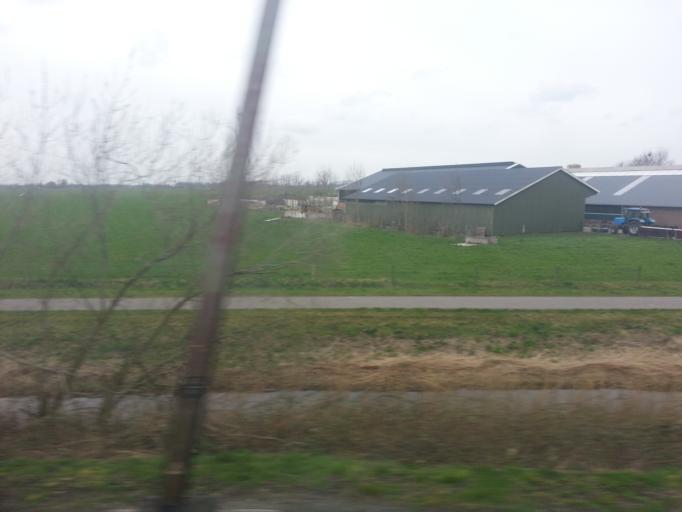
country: NL
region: Gelderland
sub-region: Gemeente Culemborg
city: Culemborg
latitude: 51.9847
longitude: 5.1942
